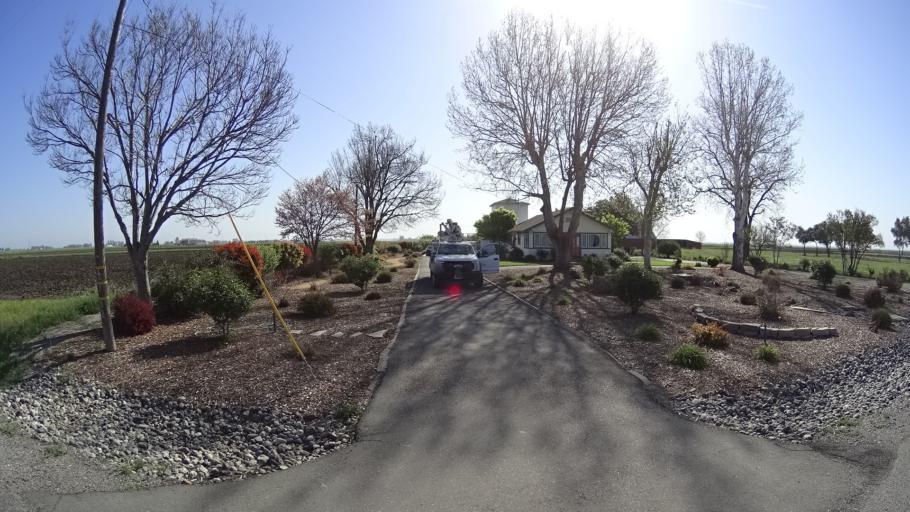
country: US
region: California
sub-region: Glenn County
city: Willows
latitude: 39.5697
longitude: -122.0839
